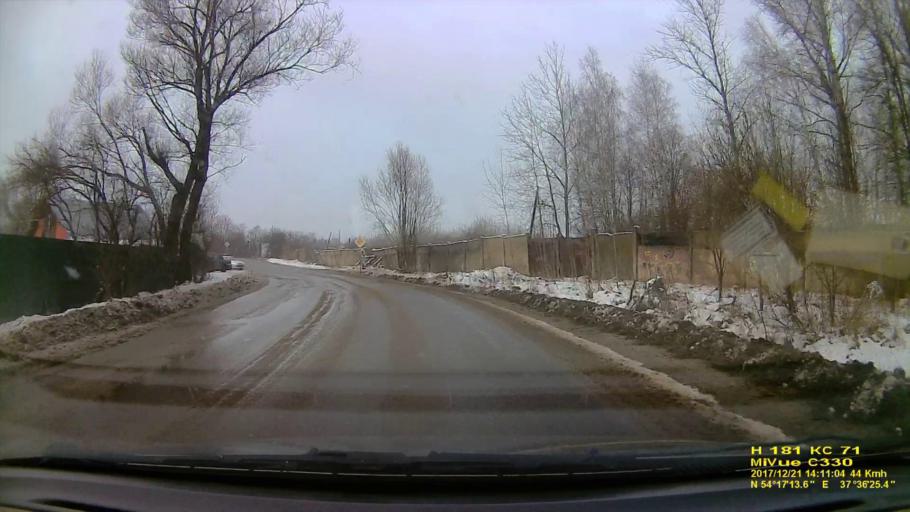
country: RU
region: Tula
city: Gorelki
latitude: 54.2874
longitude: 37.6071
